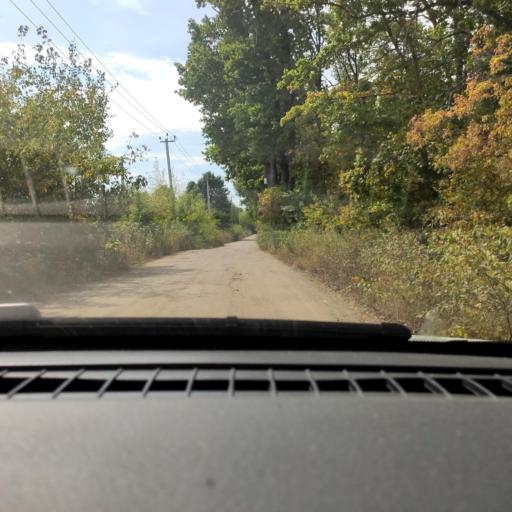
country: RU
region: Voronezj
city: Pridonskoy
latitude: 51.7533
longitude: 39.0786
